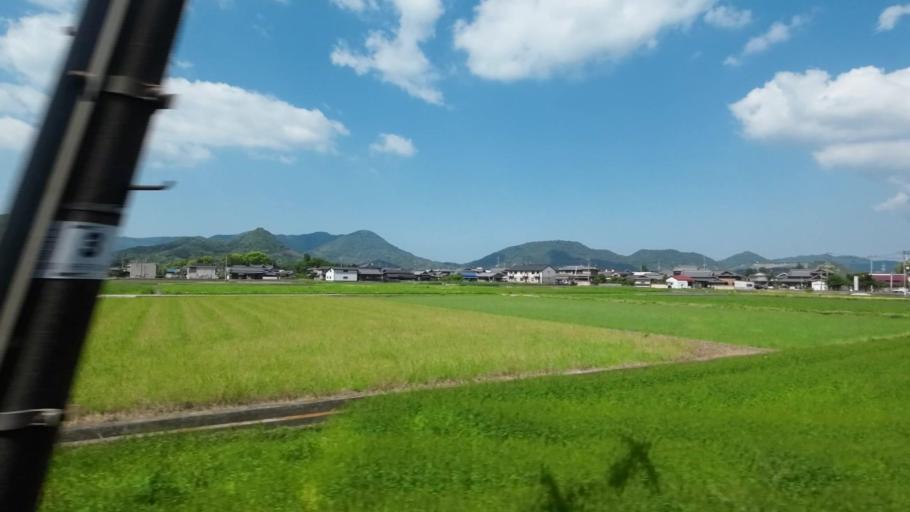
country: JP
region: Kagawa
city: Tadotsu
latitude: 34.2034
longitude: 133.7115
